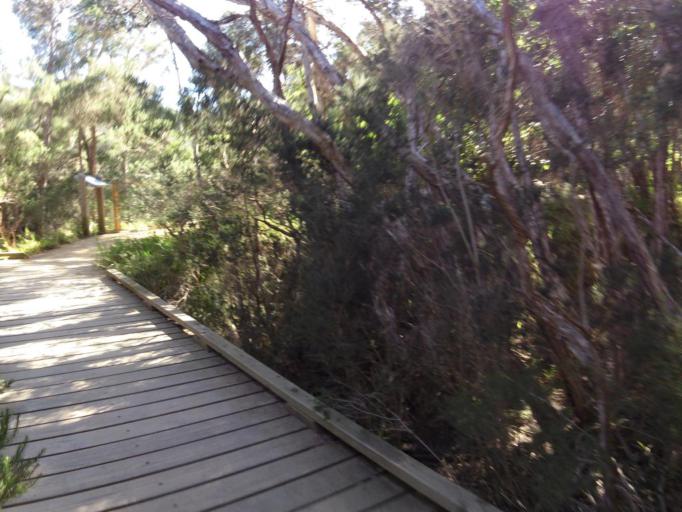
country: AU
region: Victoria
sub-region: Mornington Peninsula
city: Mount Martha
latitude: -38.2645
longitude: 145.0235
